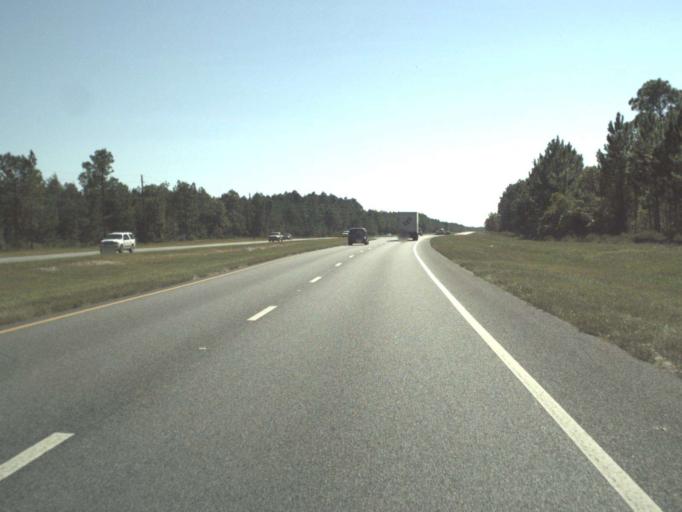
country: US
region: Florida
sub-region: Walton County
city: Seaside
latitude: 30.3498
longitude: -86.0819
